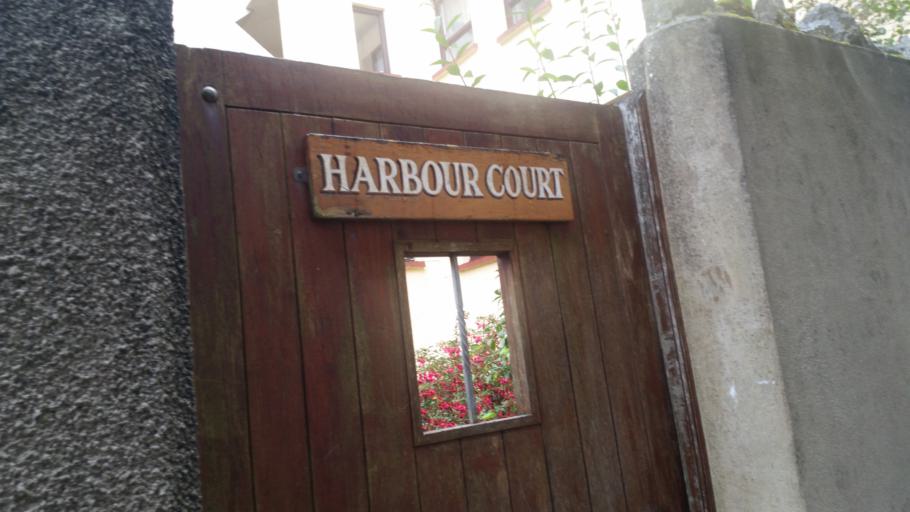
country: GB
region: Wales
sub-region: Pembrokeshire
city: Tenby
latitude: 51.6717
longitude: -4.6974
